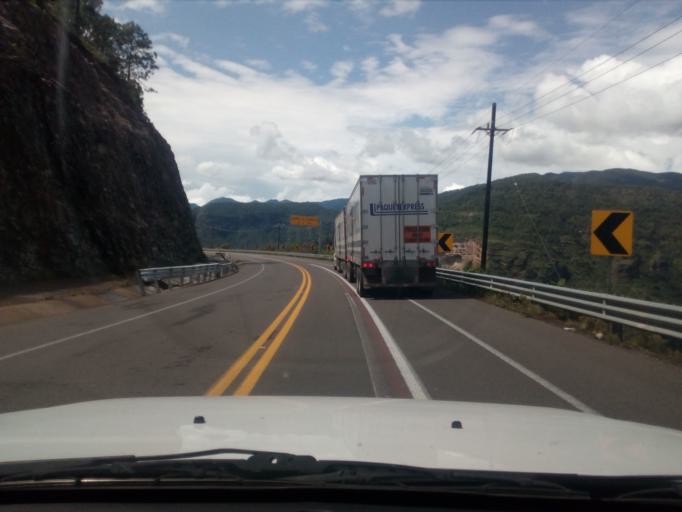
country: MX
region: Durango
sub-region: Pueblo Nuevo
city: La Ciudad
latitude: 23.6224
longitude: -105.6838
